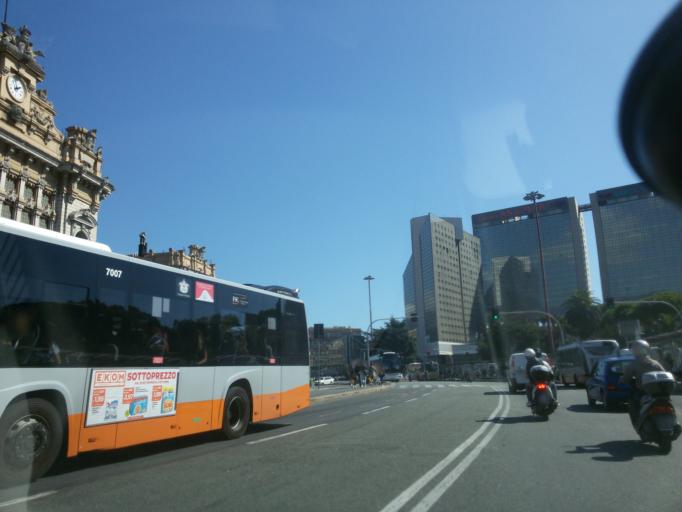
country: IT
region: Liguria
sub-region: Provincia di Genova
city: Genoa
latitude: 44.4065
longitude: 8.9459
